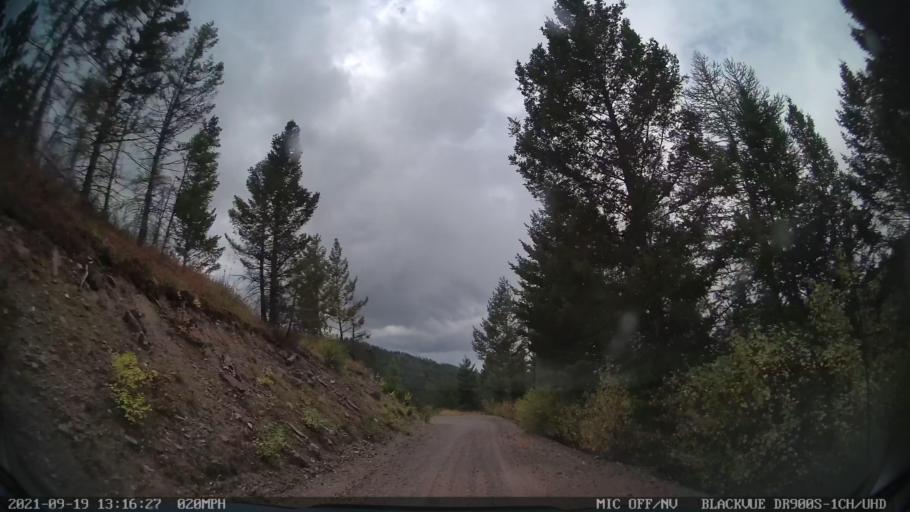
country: US
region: Montana
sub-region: Missoula County
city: Seeley Lake
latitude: 47.1777
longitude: -113.3683
